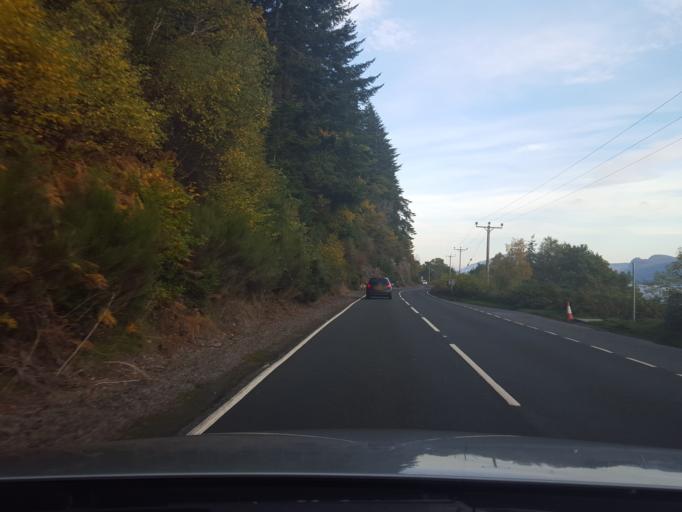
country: GB
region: Scotland
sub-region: Highland
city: Beauly
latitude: 57.2525
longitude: -4.5326
